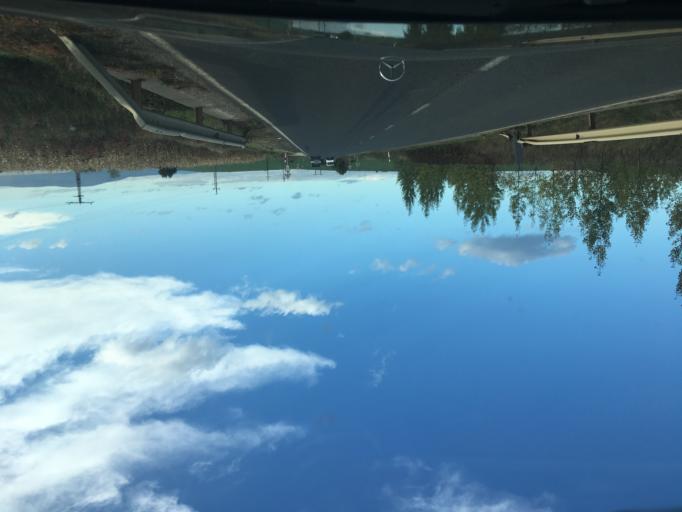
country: HU
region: Borsod-Abauj-Zemplen
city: Encs
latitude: 48.3527
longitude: 21.1265
